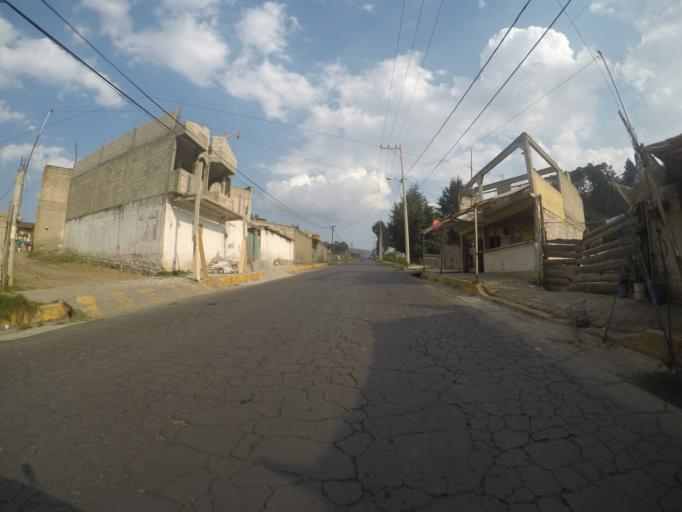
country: MX
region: Mexico
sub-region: Xalatlaco
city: El Aguila (La Mesa)
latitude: 19.1703
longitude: -99.4107
